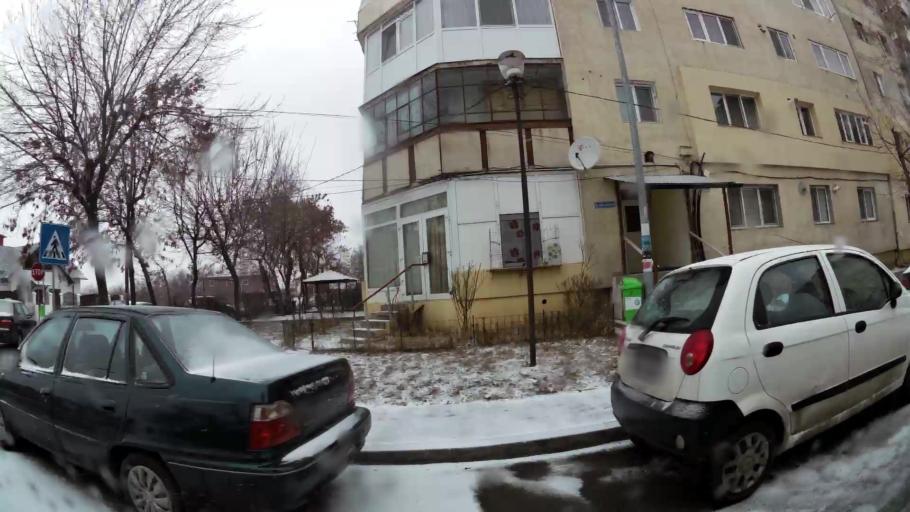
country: RO
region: Dambovita
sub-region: Municipiul Targoviste
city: Targoviste
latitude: 44.9128
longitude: 25.4747
